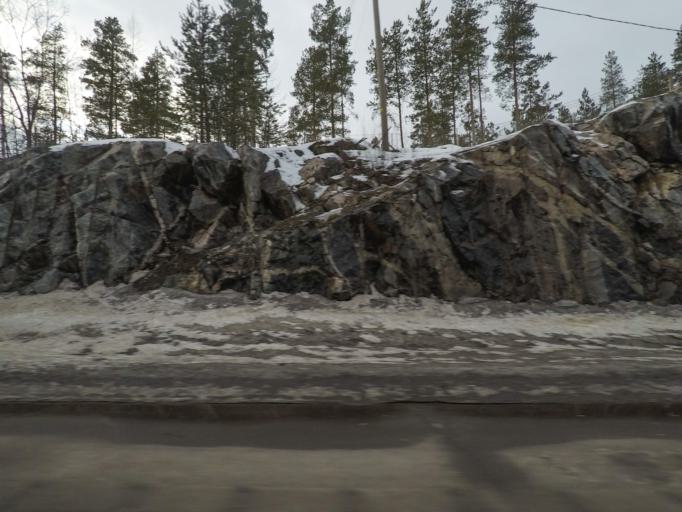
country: FI
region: Paijanne Tavastia
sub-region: Lahti
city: Heinola
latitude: 61.2297
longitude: 26.0350
